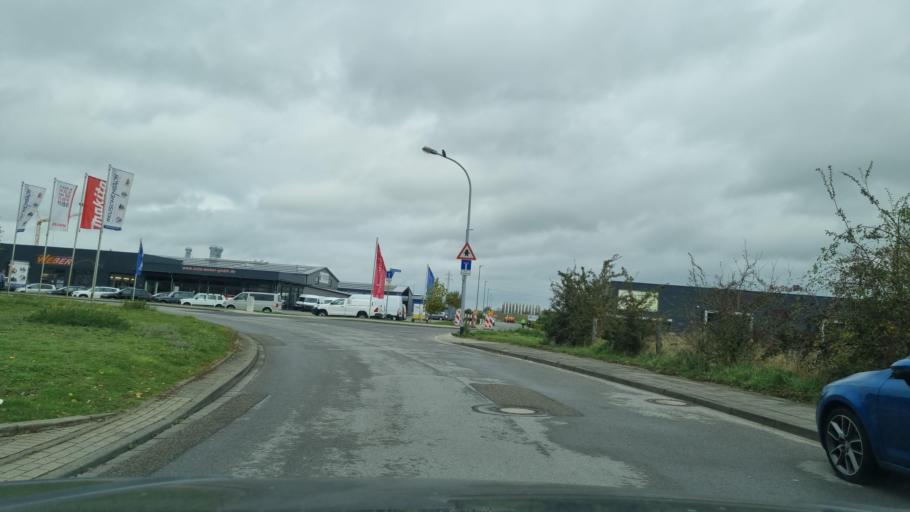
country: DE
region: North Rhine-Westphalia
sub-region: Regierungsbezirk Dusseldorf
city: Kleve
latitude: 51.8130
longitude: 6.1422
